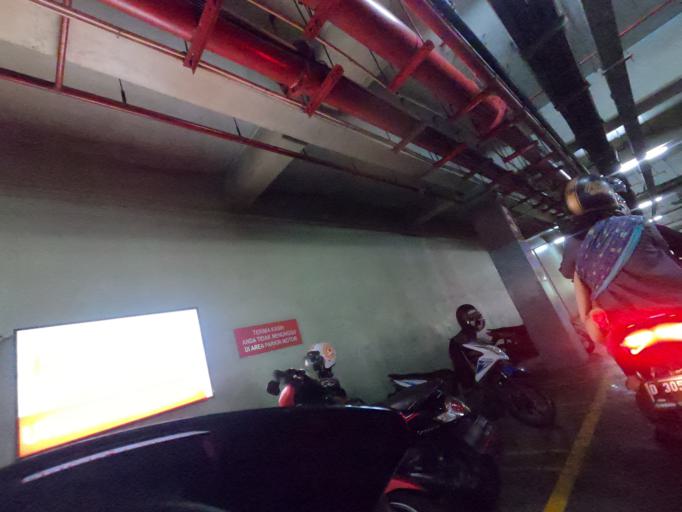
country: ID
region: West Java
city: Bandung
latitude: -6.8936
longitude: 107.6018
